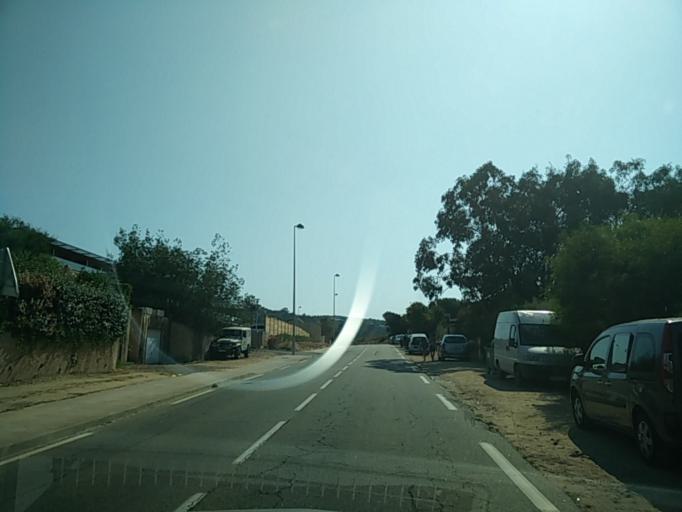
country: FR
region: Corsica
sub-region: Departement de la Corse-du-Sud
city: Pietrosella
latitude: 41.8499
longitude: 8.7882
